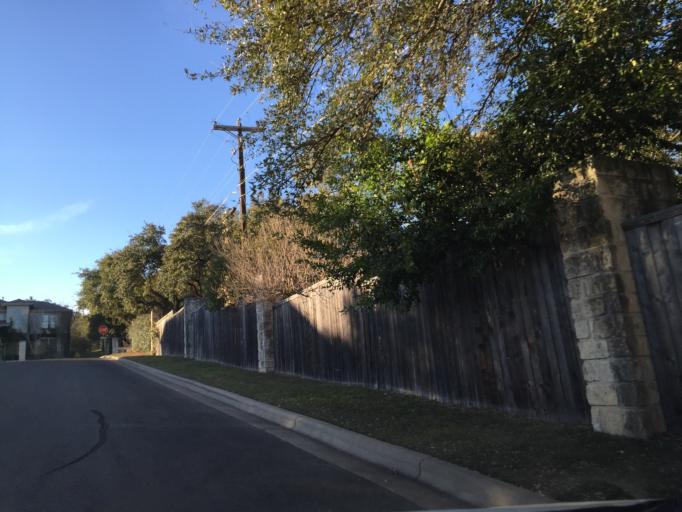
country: US
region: Texas
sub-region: Travis County
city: Rollingwood
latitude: 30.2725
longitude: -97.8196
